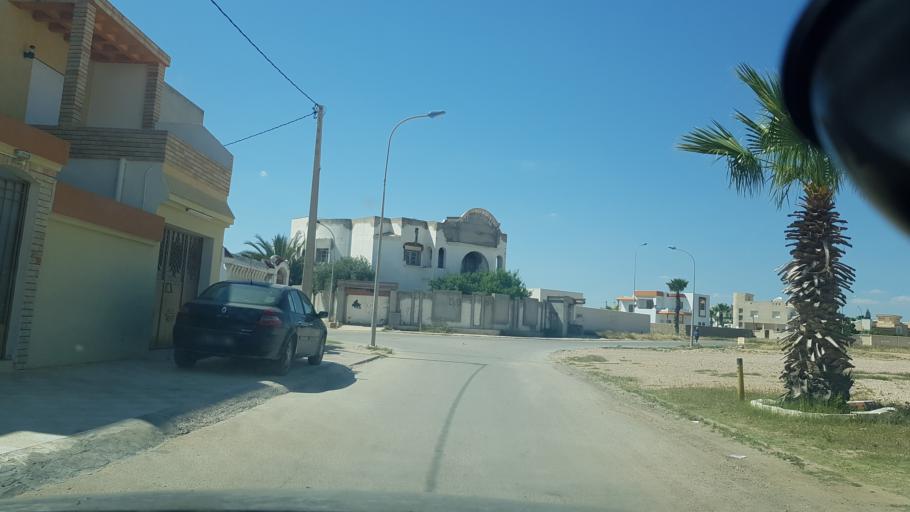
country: TN
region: Safaqis
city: Al Qarmadah
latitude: 34.8266
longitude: 10.7565
